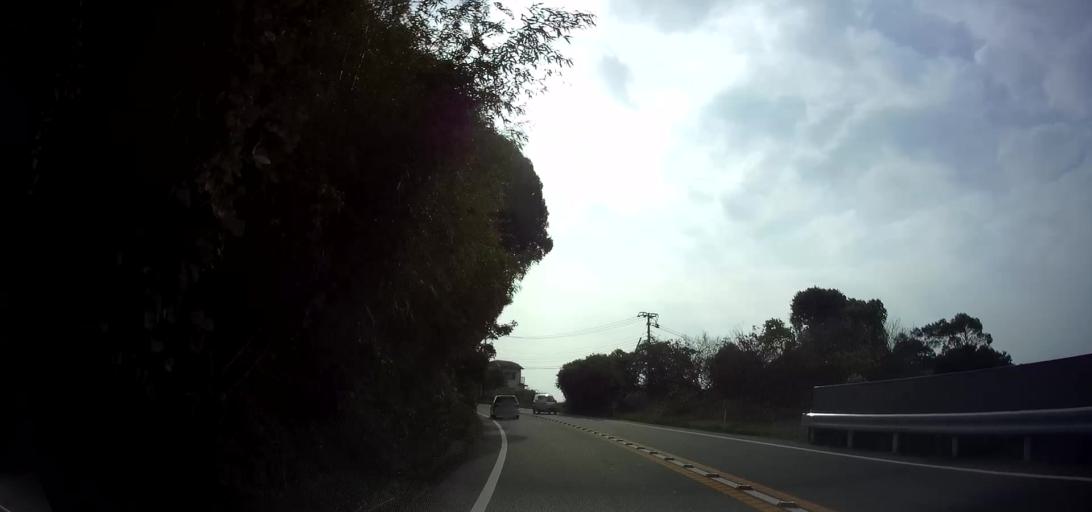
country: JP
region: Nagasaki
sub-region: Isahaya-shi
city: Isahaya
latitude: 32.7974
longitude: 130.1340
